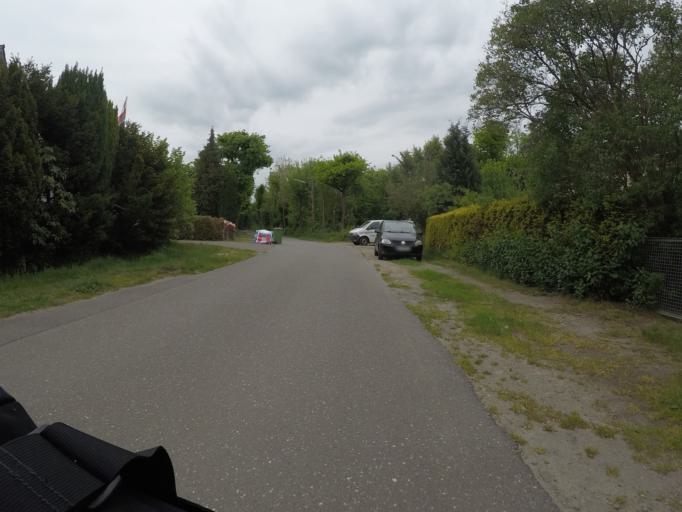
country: DE
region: Hamburg
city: Langenhorn
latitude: 53.6429
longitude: 9.9802
